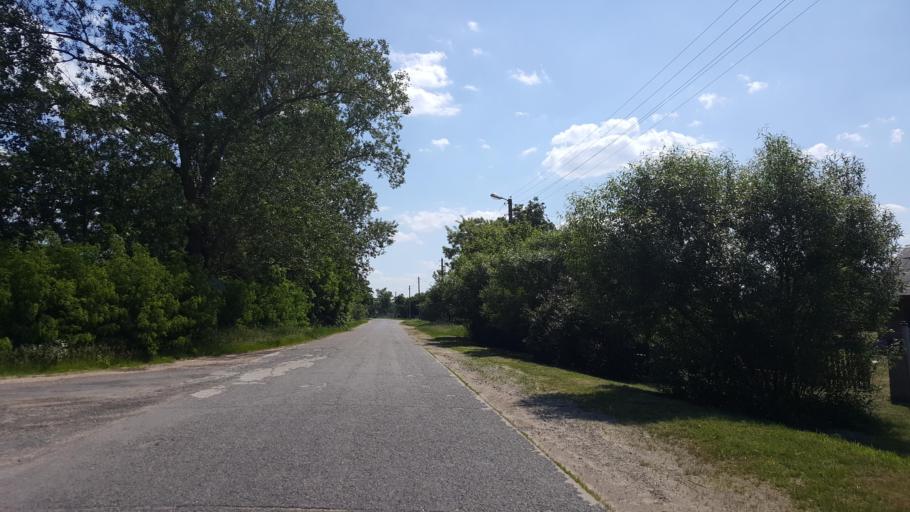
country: BY
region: Brest
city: Zhabinka
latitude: 52.2431
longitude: 24.0295
